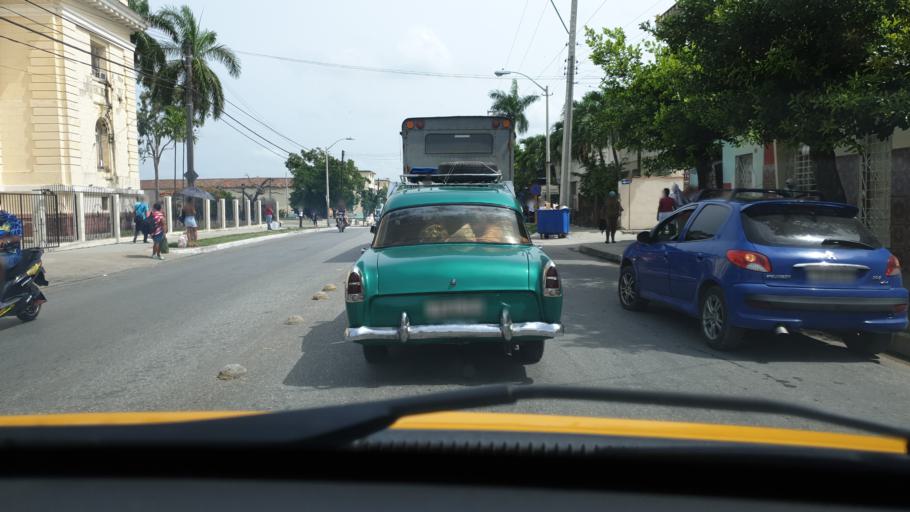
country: CU
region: Villa Clara
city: Santa Clara
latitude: 22.3991
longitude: -79.9636
